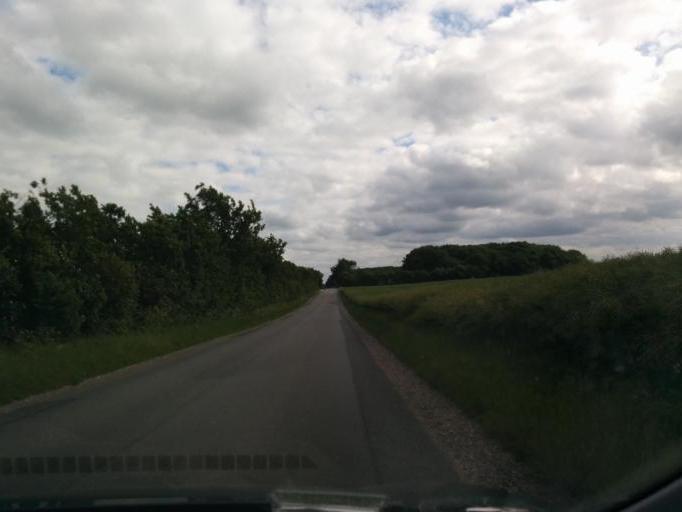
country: DK
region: Central Jutland
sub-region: Norddjurs Kommune
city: Grenaa
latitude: 56.4619
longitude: 10.7137
